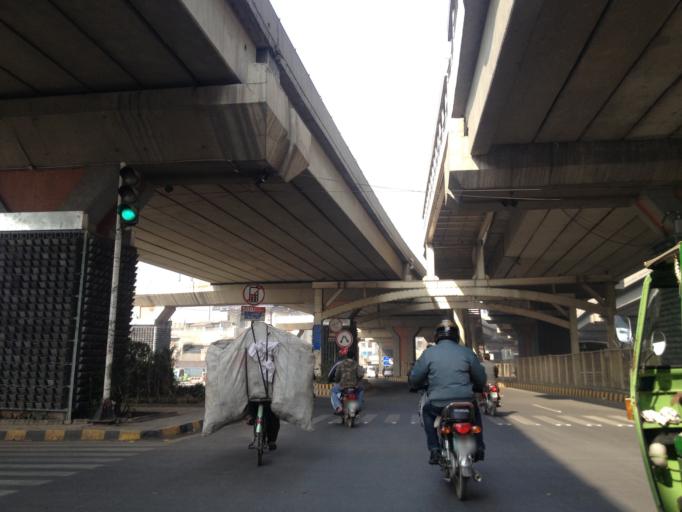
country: PK
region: Punjab
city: Lahore
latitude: 31.5198
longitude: 74.3261
